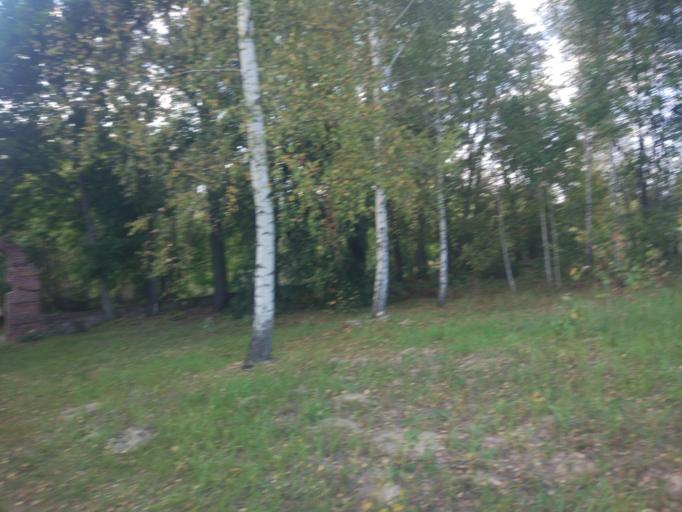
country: RU
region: Brjansk
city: Vyshkov
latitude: 52.6679
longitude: 31.5566
